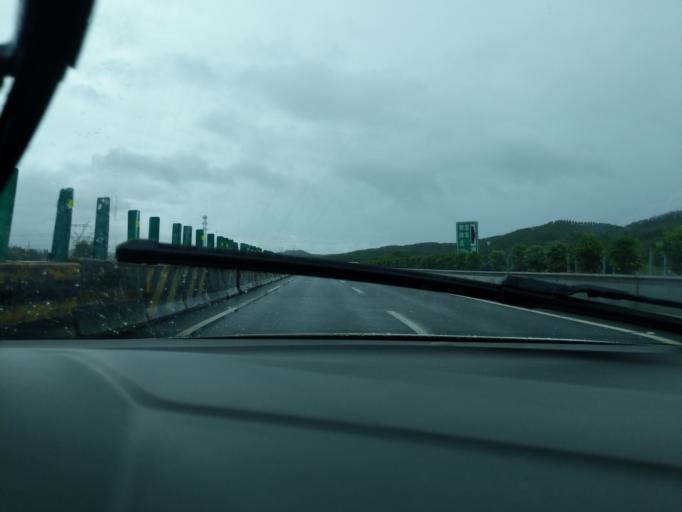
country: CN
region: Guangdong
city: Liangxi
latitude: 22.2711
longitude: 112.3276
